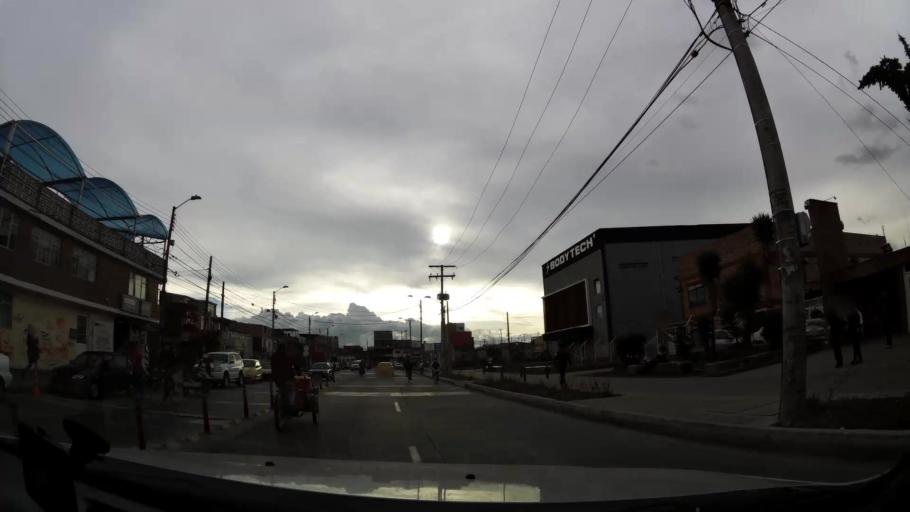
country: CO
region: Cundinamarca
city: Soacha
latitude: 4.6184
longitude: -74.1590
